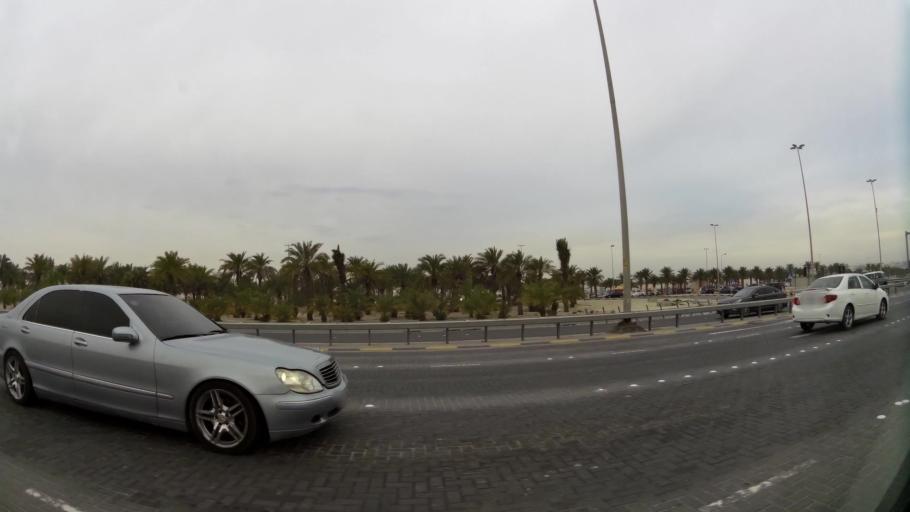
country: BH
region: Northern
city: Ar Rifa'
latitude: 26.1033
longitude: 50.5647
